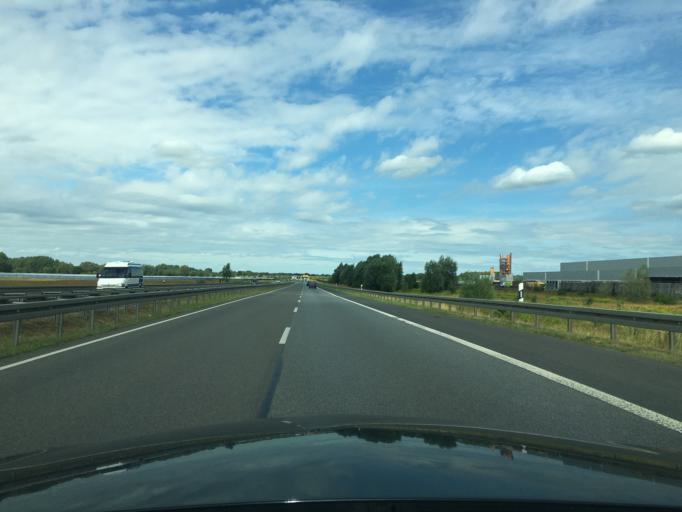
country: DE
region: Brandenburg
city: Leegebruch
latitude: 52.7264
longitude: 13.2160
